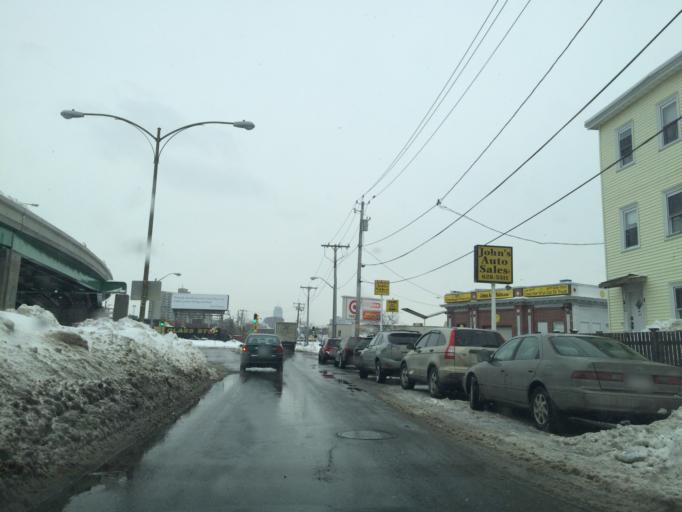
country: US
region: Massachusetts
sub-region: Middlesex County
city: Somerville
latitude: 42.3781
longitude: -71.0895
